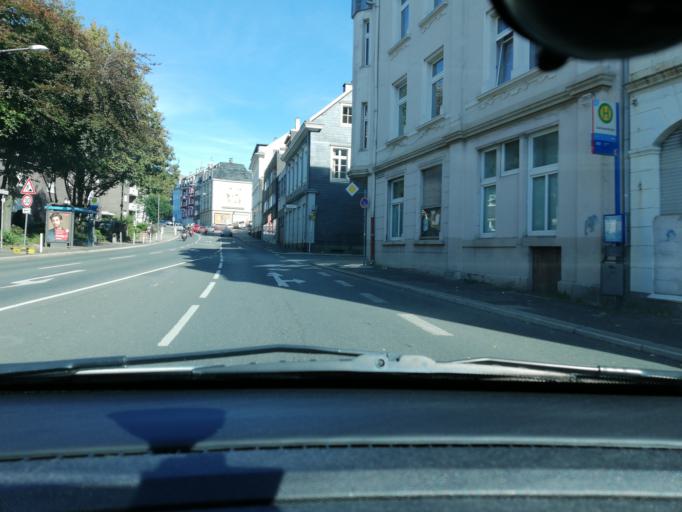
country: DE
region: North Rhine-Westphalia
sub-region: Regierungsbezirk Dusseldorf
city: Wuppertal
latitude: 51.2831
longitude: 7.2090
